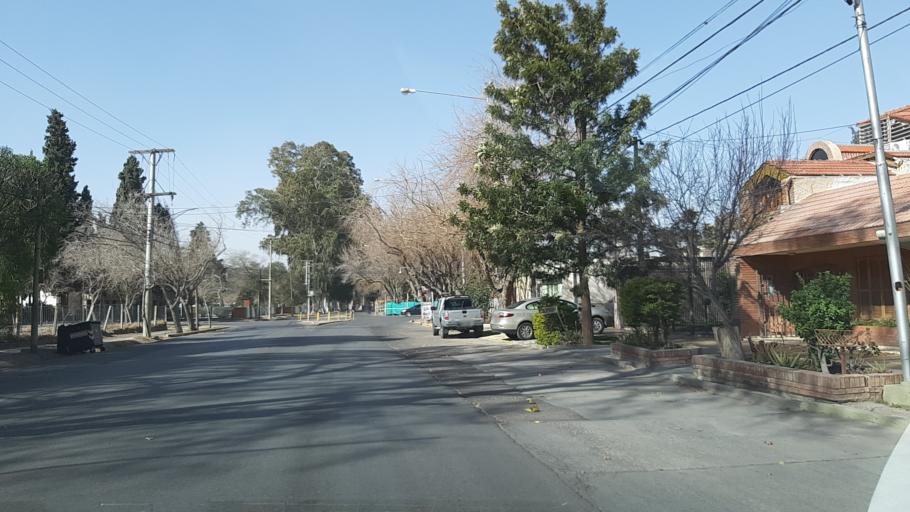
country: AR
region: San Juan
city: San Juan
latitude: -31.5291
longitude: -68.5452
